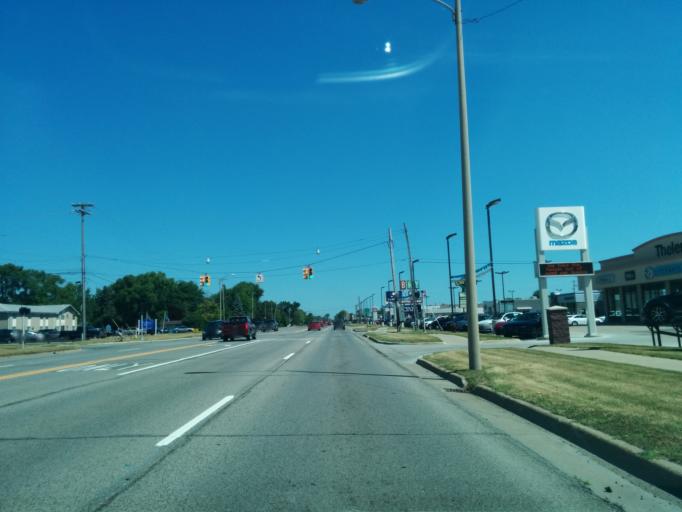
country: US
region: Michigan
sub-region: Bay County
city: Bay City
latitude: 43.6159
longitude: -83.9145
